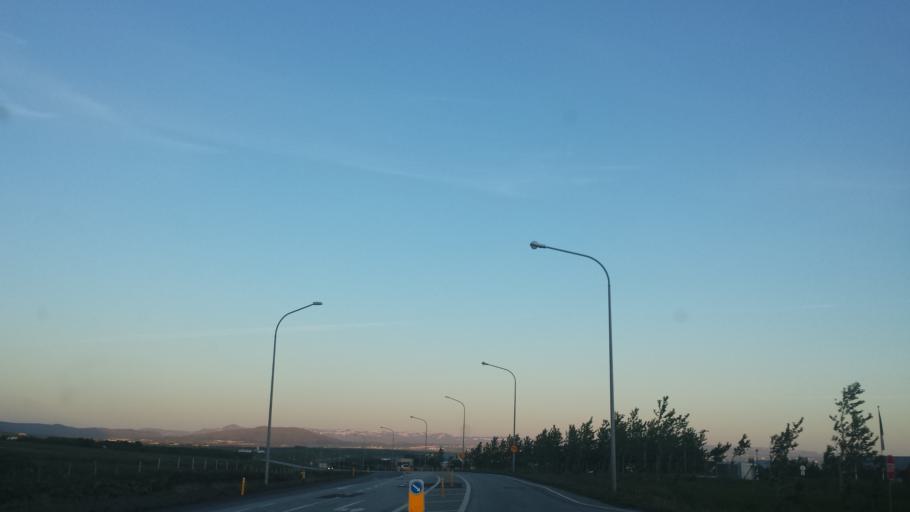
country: IS
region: Capital Region
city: Reykjavik
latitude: 64.2429
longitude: -21.8295
